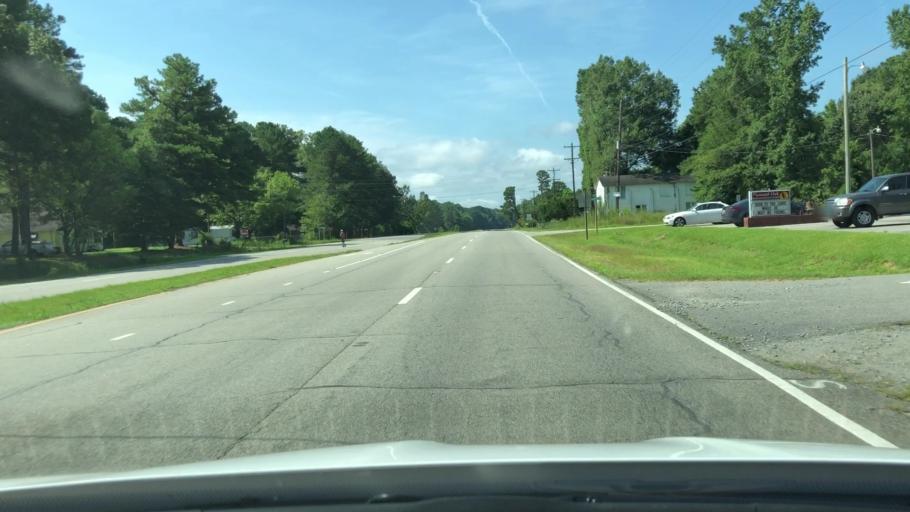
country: US
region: North Carolina
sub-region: Bertie County
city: Windsor
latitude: 35.9524
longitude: -76.9557
